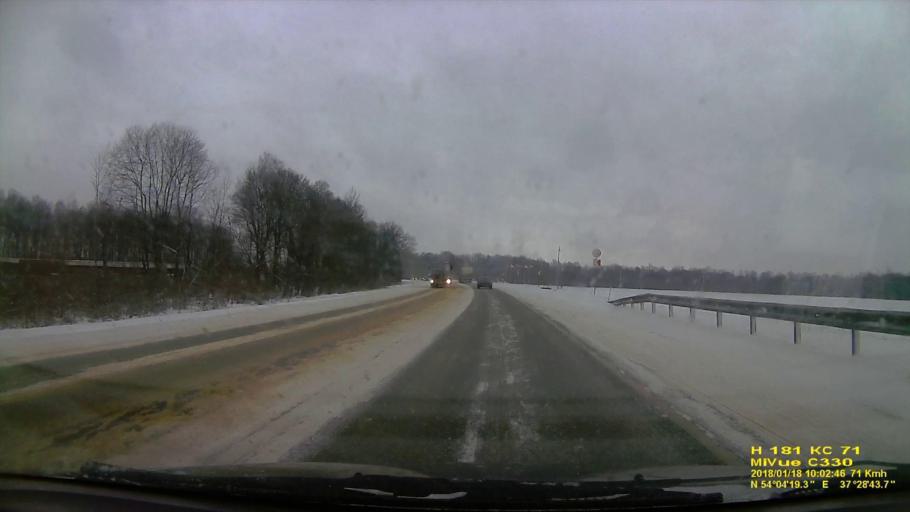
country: RU
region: Tula
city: Pervomayskiy
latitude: 54.0718
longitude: 37.4787
